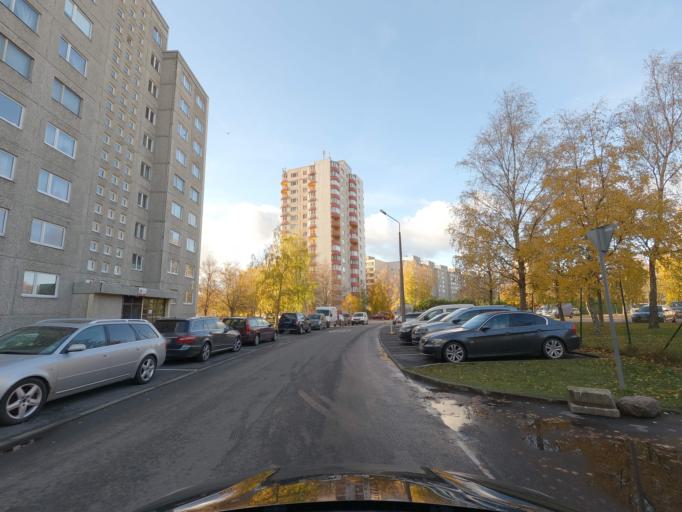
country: EE
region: Harju
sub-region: Saue vald
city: Laagri
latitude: 59.4129
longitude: 24.6447
